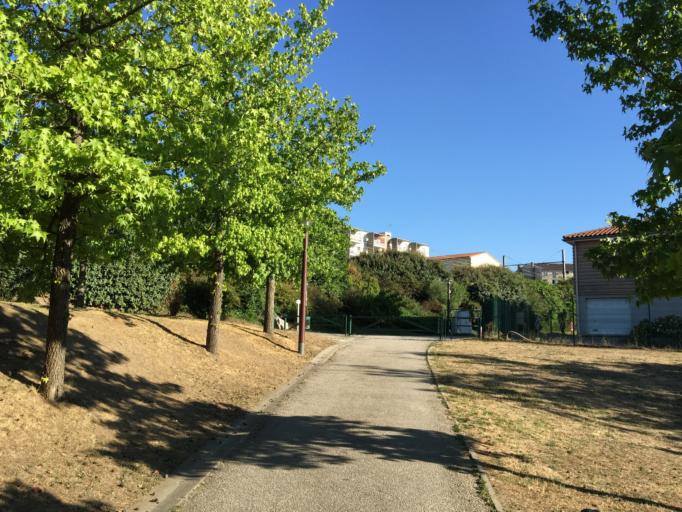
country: FR
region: Rhone-Alpes
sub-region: Departement de la Loire
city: Lorette
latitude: 45.4985
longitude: 4.5638
